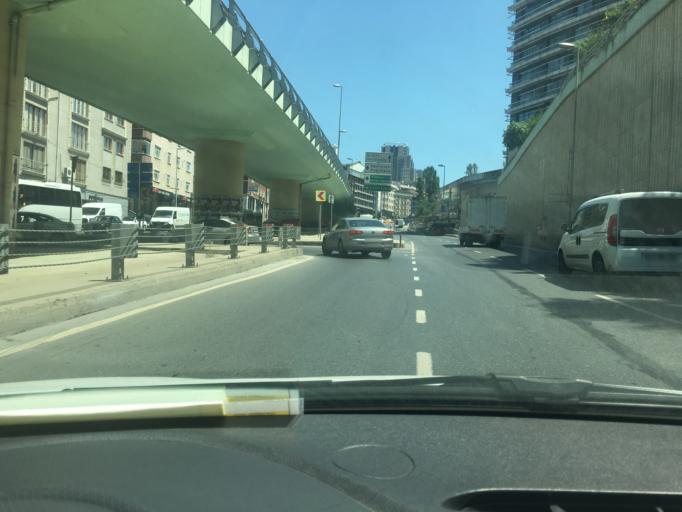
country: TR
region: Istanbul
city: Sisli
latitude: 41.0595
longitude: 28.9770
